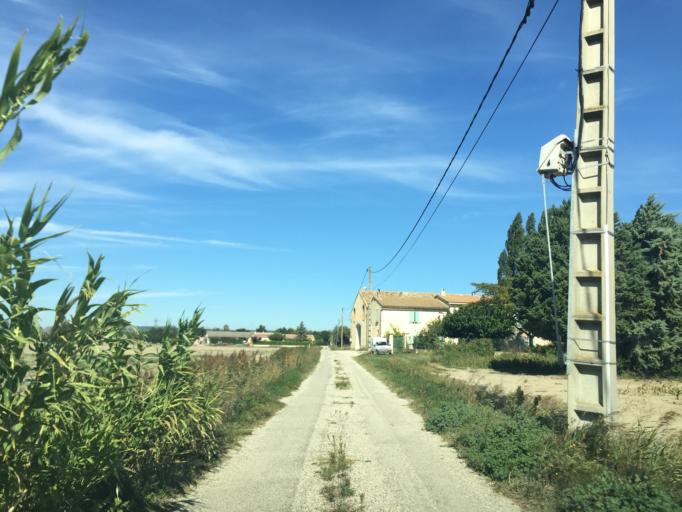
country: FR
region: Provence-Alpes-Cote d'Azur
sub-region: Departement du Vaucluse
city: Piolenc
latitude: 44.1514
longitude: 4.7412
